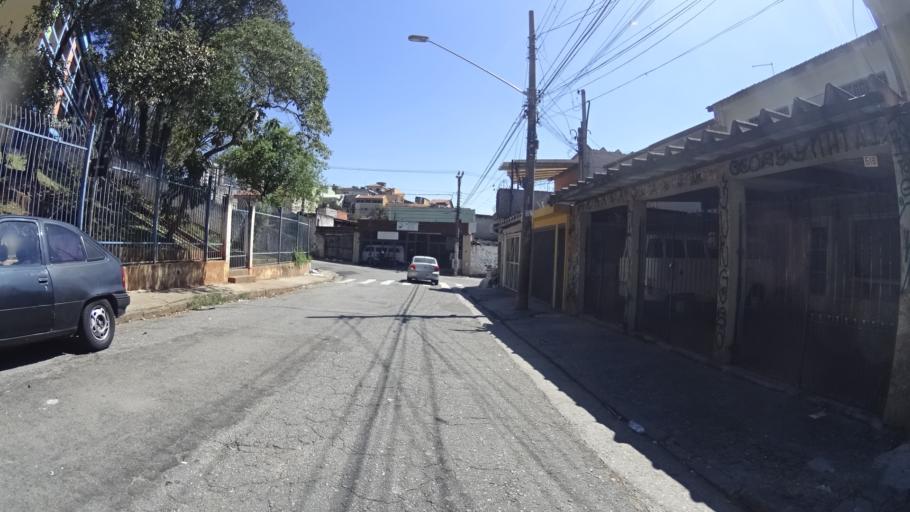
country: BR
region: Sao Paulo
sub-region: Sao Paulo
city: Sao Paulo
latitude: -23.4857
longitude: -46.6705
